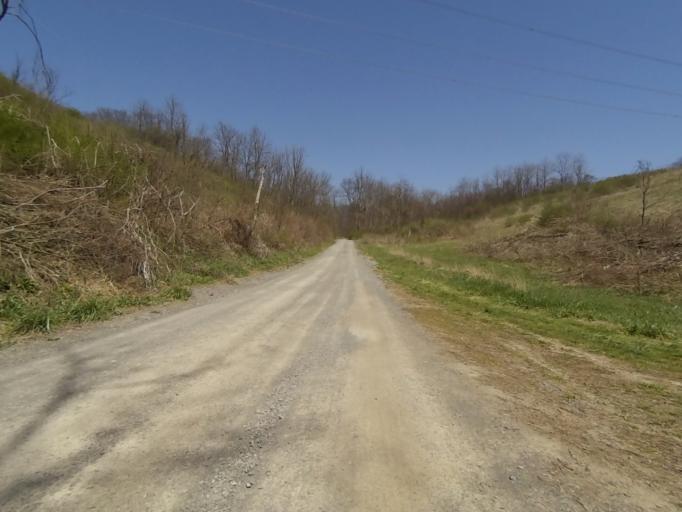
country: US
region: Pennsylvania
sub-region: Blair County
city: Williamsburg
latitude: 40.5432
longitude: -78.1568
